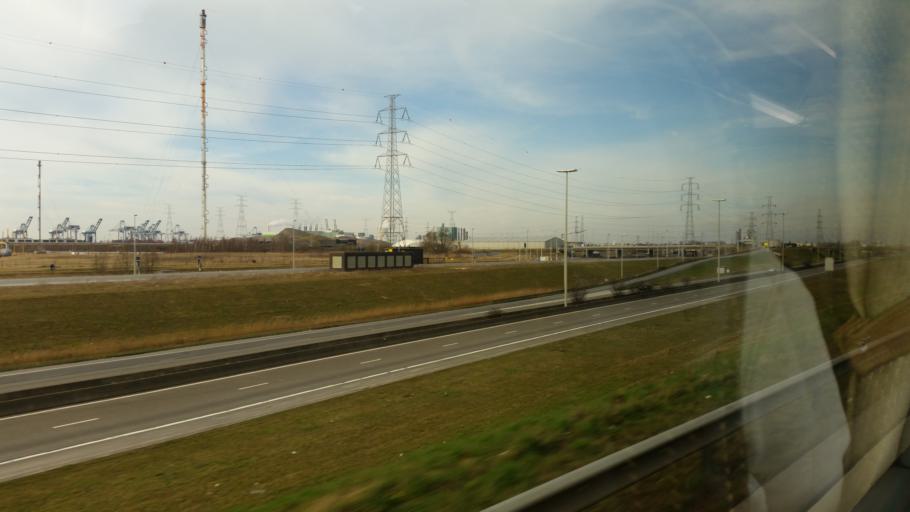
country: BE
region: Flanders
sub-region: Provincie Oost-Vlaanderen
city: Beveren
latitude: 51.2728
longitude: 4.2796
